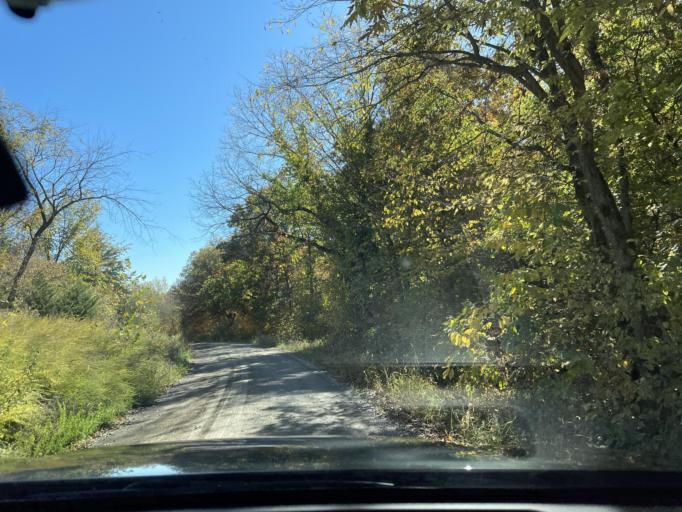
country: US
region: Missouri
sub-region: Andrew County
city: Savannah
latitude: 39.9384
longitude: -94.8687
